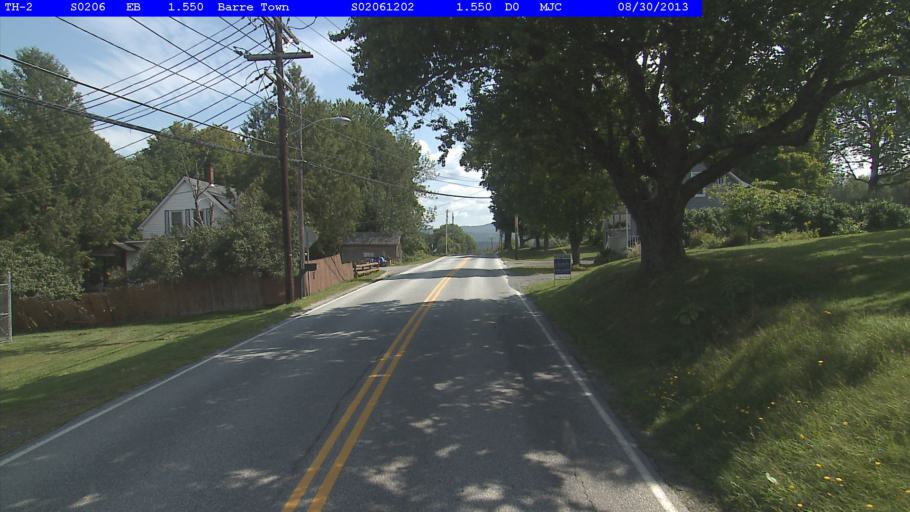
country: US
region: Vermont
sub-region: Washington County
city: South Barre
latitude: 44.1614
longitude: -72.4658
